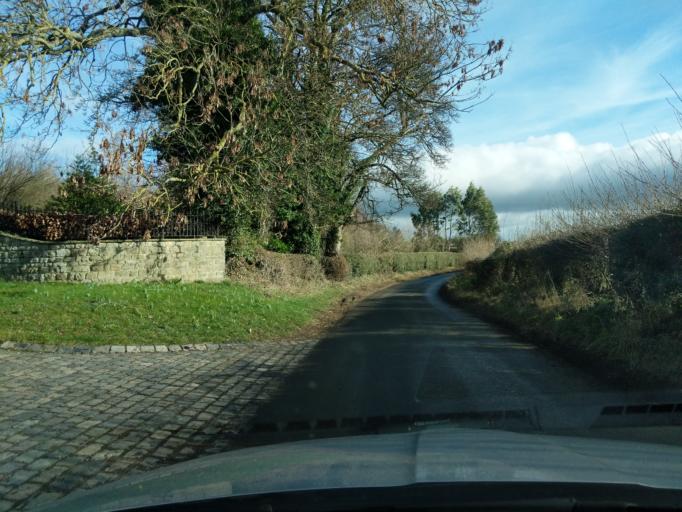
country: GB
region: England
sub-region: North Yorkshire
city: Catterick Garrison
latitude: 54.3320
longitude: -1.7053
